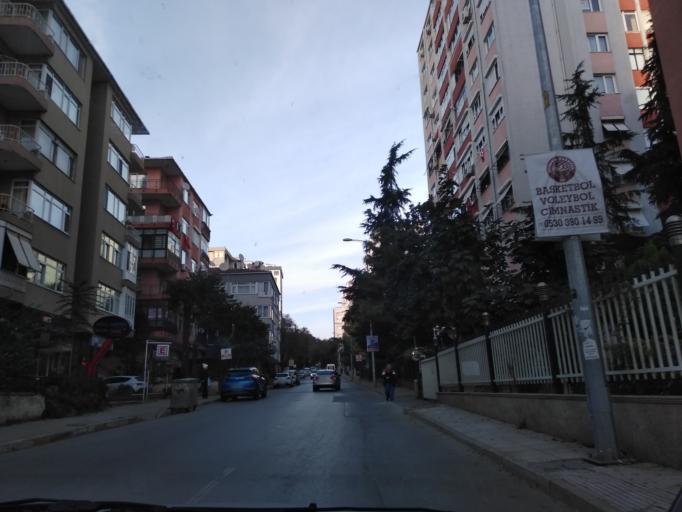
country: TR
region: Istanbul
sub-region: Atasehir
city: Atasehir
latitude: 40.9698
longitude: 29.0896
